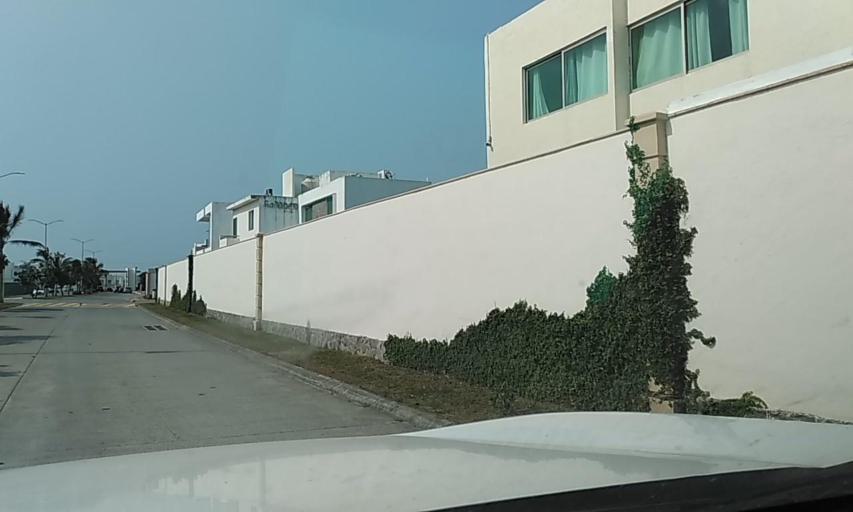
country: MX
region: Veracruz
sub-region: Alvarado
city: Playa de la Libertad
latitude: 19.0541
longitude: -96.0612
